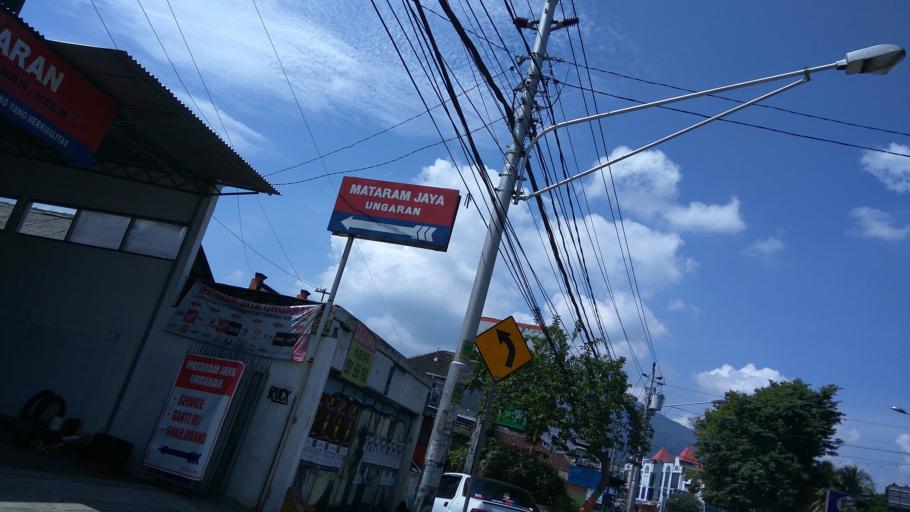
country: ID
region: Central Java
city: Ungaran
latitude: -7.1220
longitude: 110.4080
